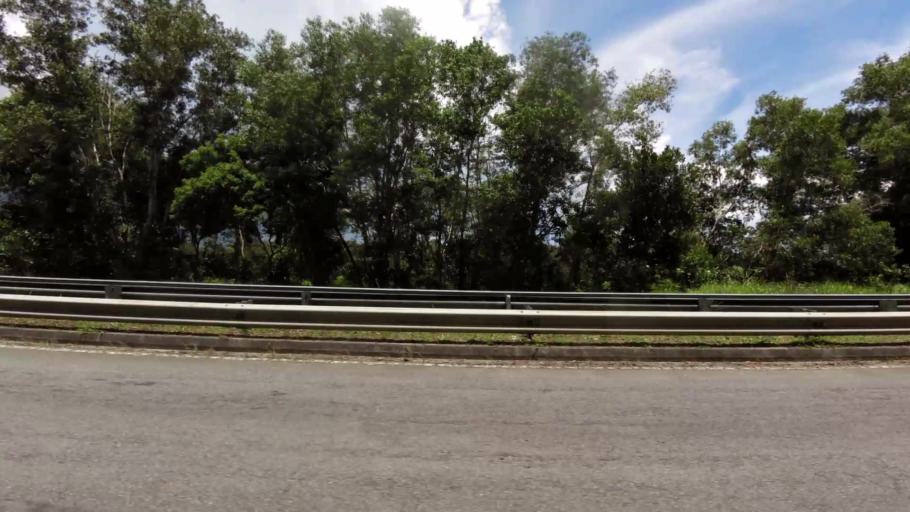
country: BN
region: Brunei and Muara
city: Bandar Seri Begawan
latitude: 4.9508
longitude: 114.9039
